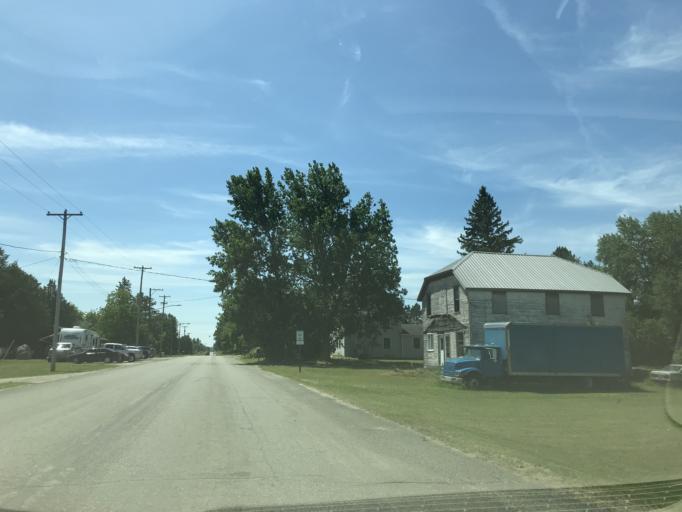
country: US
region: Michigan
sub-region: Roscommon County
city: Houghton Lake
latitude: 44.3311
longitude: -84.9446
